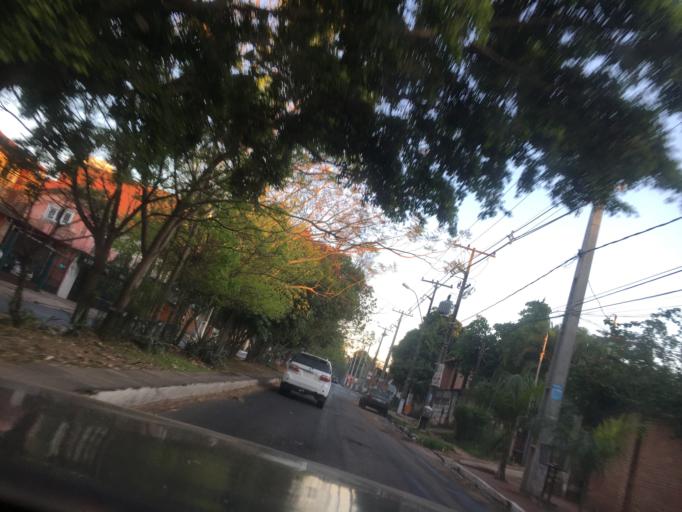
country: PY
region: Central
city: Lambare
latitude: -25.3374
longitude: -57.6062
